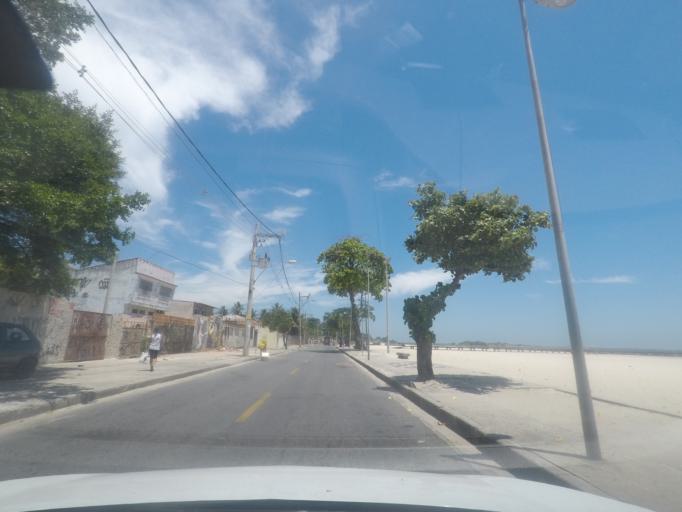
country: BR
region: Rio de Janeiro
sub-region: Itaguai
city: Itaguai
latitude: -22.9734
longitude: -43.7078
